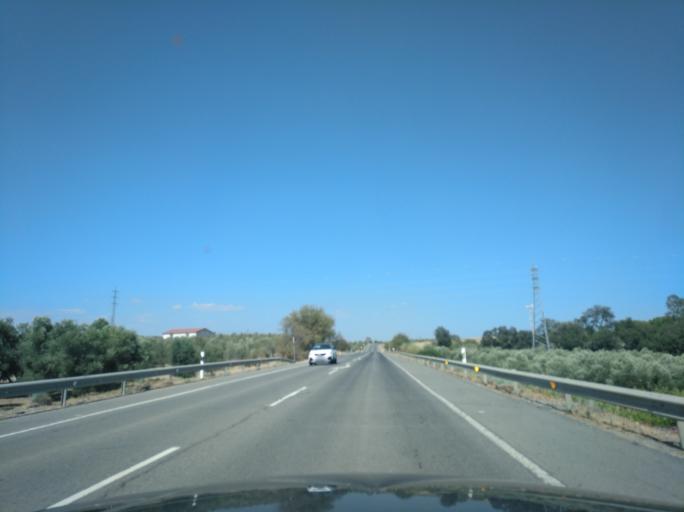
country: ES
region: Andalusia
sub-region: Provincia de Huelva
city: Gibraleon
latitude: 37.3456
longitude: -7.0198
